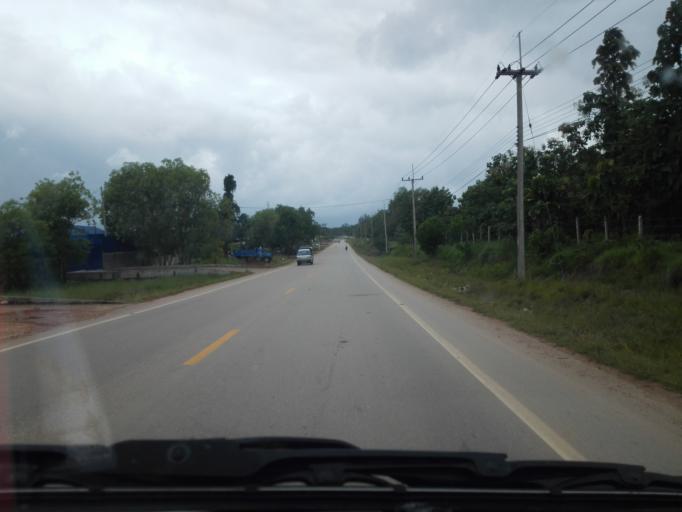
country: TH
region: Tak
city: Mae Sot
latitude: 16.6919
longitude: 98.4554
